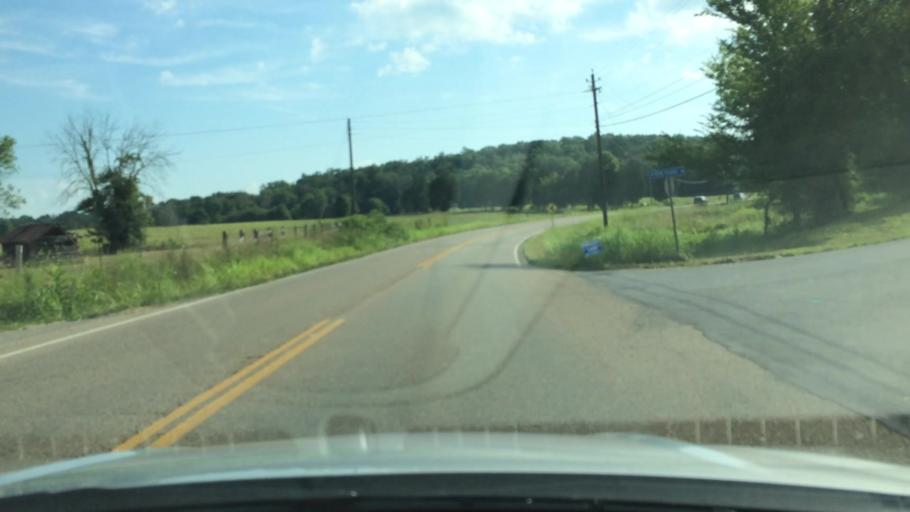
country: US
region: Tennessee
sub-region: Sevier County
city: Sevierville
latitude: 35.9196
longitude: -83.6194
